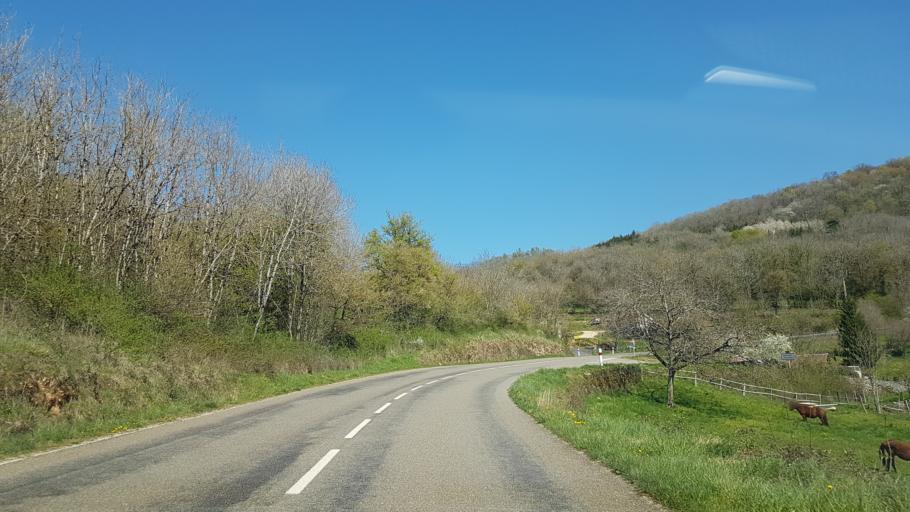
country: FR
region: Bourgogne
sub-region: Departement de Saone-et-Loire
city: Cuiseaux
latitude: 46.4601
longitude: 5.3852
